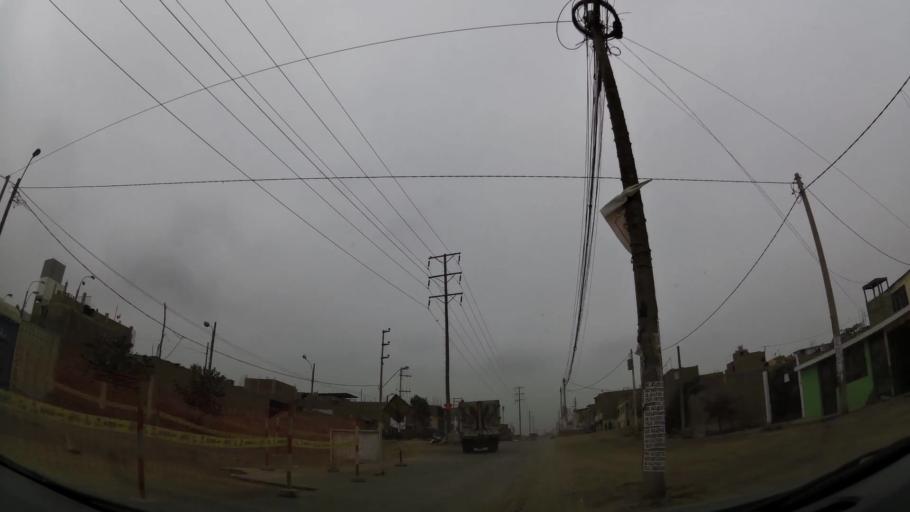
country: PE
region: Lima
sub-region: Lima
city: Surco
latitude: -12.1976
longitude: -76.9685
